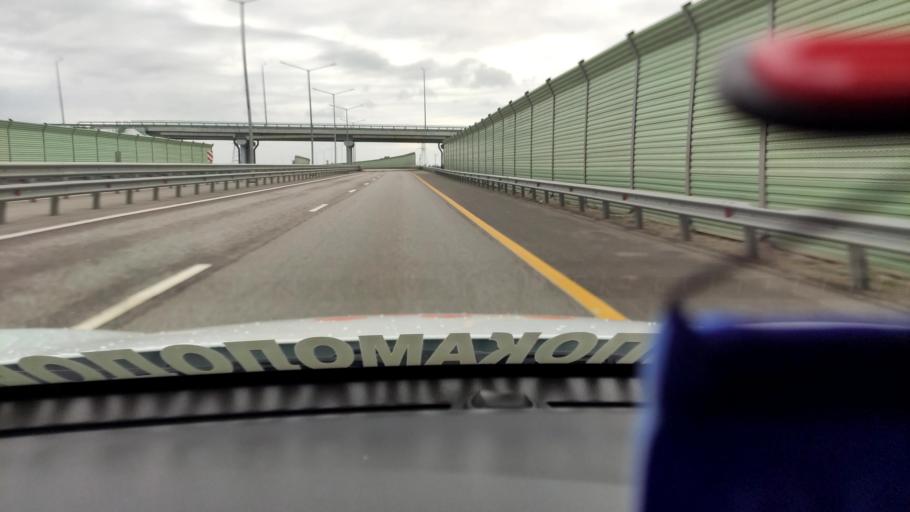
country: RU
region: Voronezj
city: Novaya Usman'
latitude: 51.6154
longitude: 39.3194
